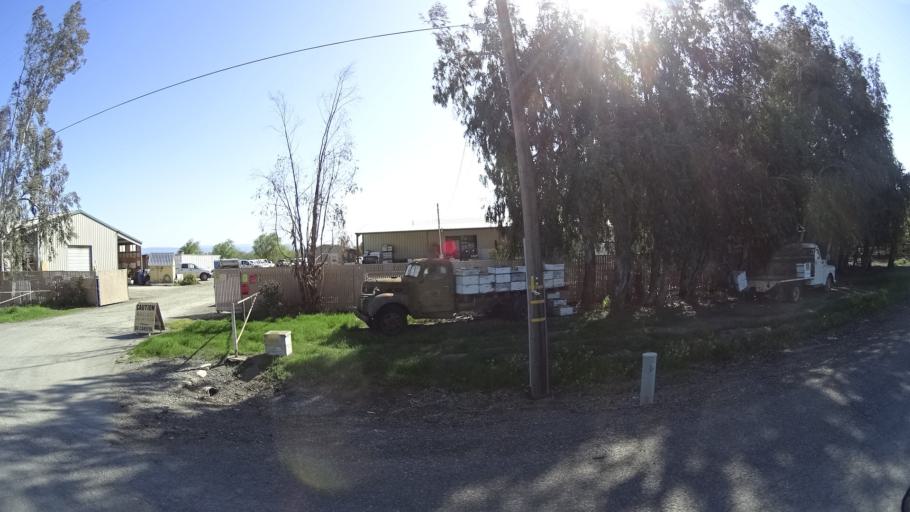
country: US
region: California
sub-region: Glenn County
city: Hamilton City
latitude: 39.7713
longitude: -122.0477
